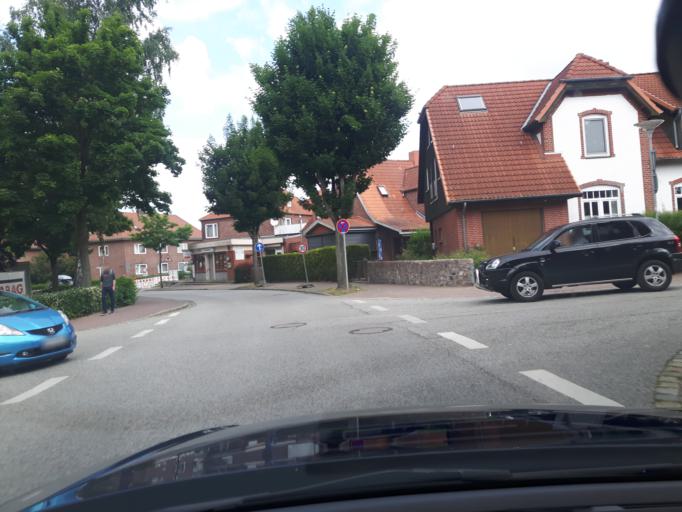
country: DE
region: Schleswig-Holstein
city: Neustadt in Holstein
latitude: 54.1036
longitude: 10.8175
